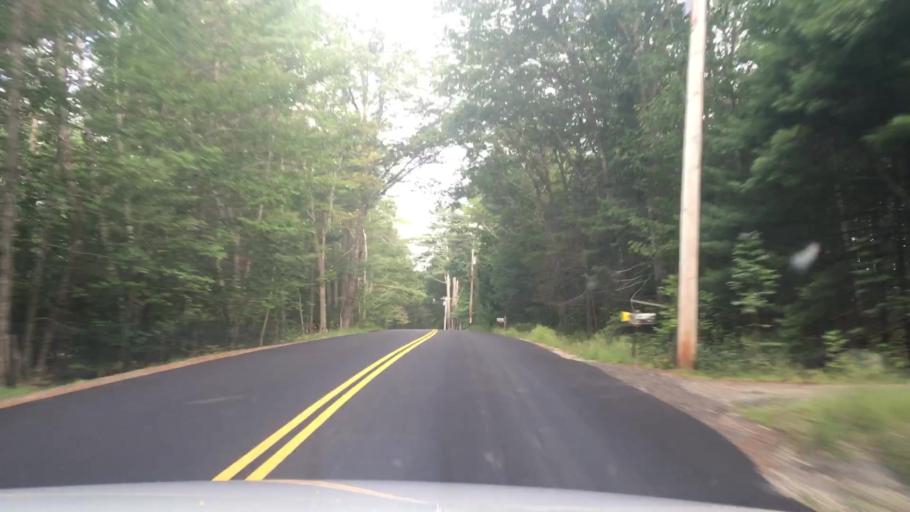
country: US
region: Maine
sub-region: Androscoggin County
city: Lisbon Falls
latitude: 44.0445
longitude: -70.0499
